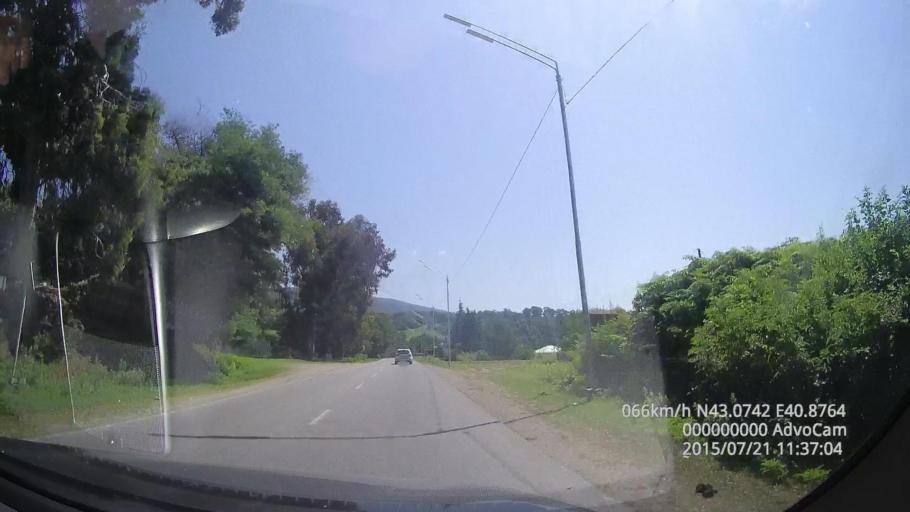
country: GE
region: Abkhazia
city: Stantsiya Novyy Afon
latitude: 43.0742
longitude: 40.8770
